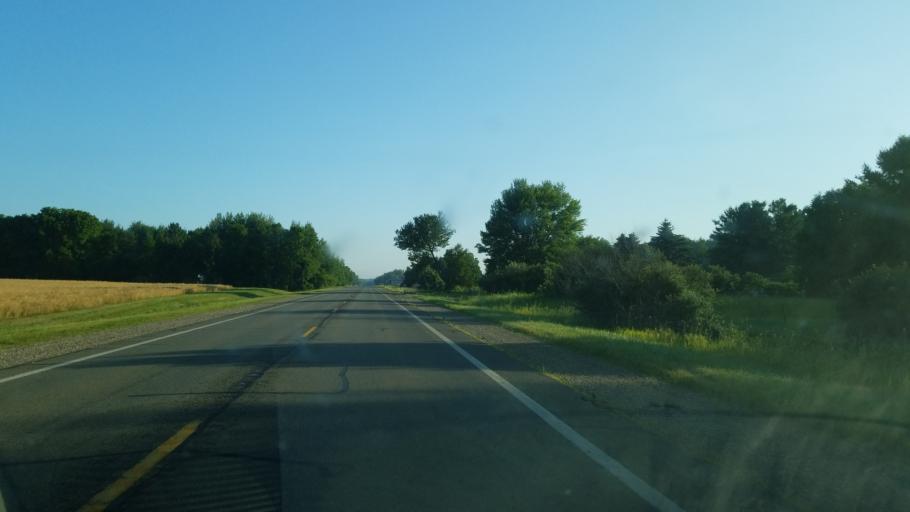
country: US
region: Michigan
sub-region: Montcalm County
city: Edmore
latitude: 43.3952
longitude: -85.0847
